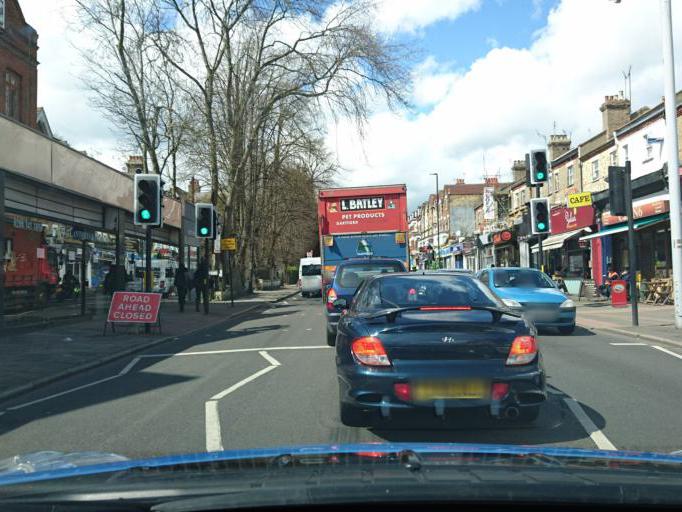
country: GB
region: England
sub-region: Greater London
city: Crouch End
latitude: 51.5738
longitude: -0.1414
